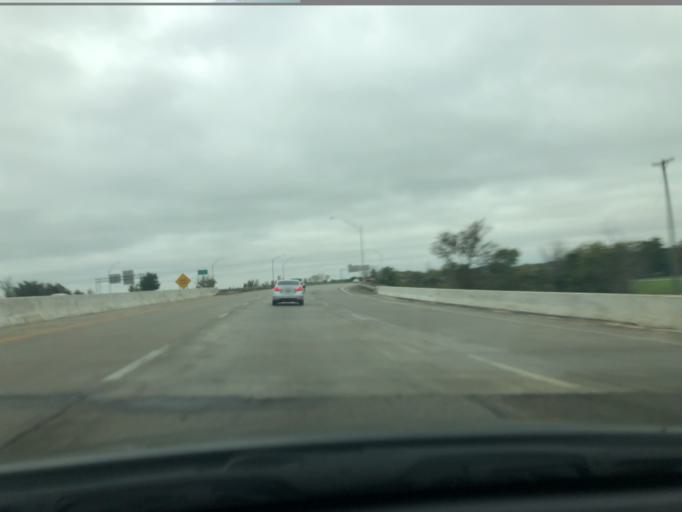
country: US
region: Ohio
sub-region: Union County
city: Marysville
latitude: 40.2425
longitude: -83.3982
